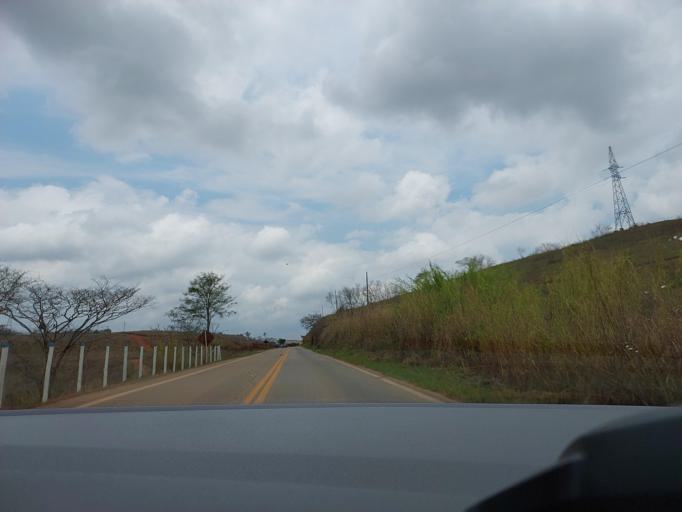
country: BR
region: Minas Gerais
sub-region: Ponte Nova
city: Ponte Nova
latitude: -20.3862
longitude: -42.8716
